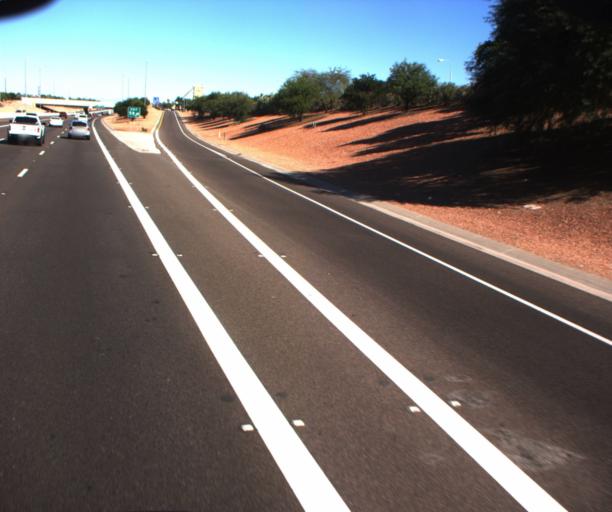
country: US
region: Arizona
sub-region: Maricopa County
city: San Carlos
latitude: 33.3154
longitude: -111.8942
